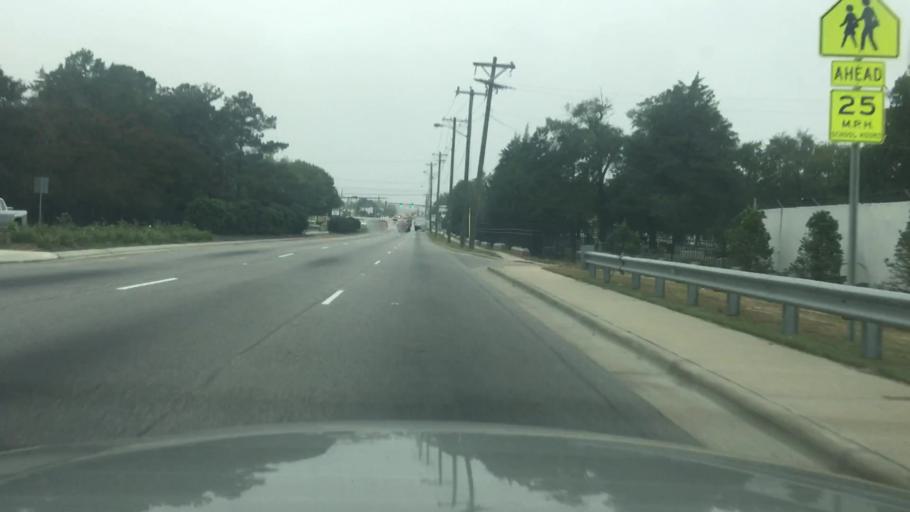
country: US
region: North Carolina
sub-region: Cumberland County
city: Fayetteville
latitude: 35.0558
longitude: -78.8725
